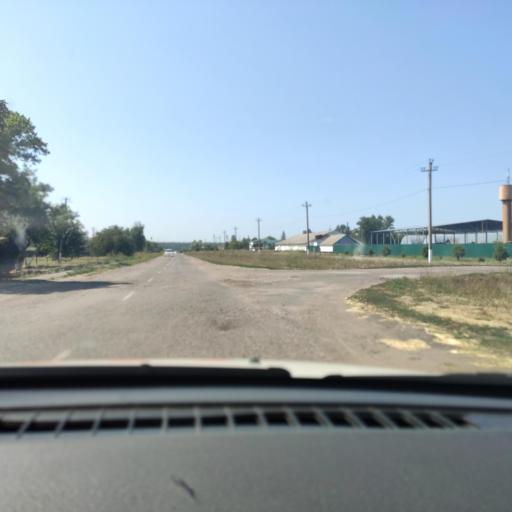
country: RU
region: Voronezj
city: Imeni Pervogo Maya
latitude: 50.7181
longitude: 39.3873
